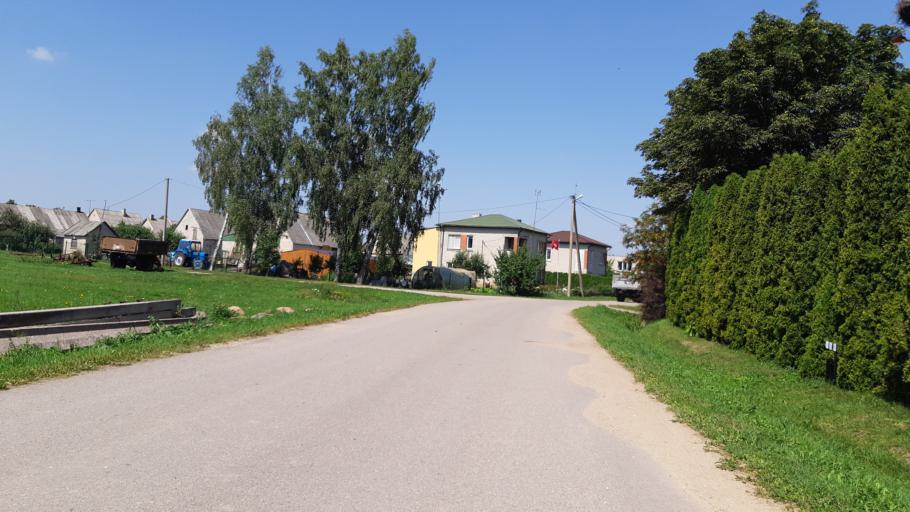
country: LT
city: Virbalis
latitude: 54.6205
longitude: 22.8164
